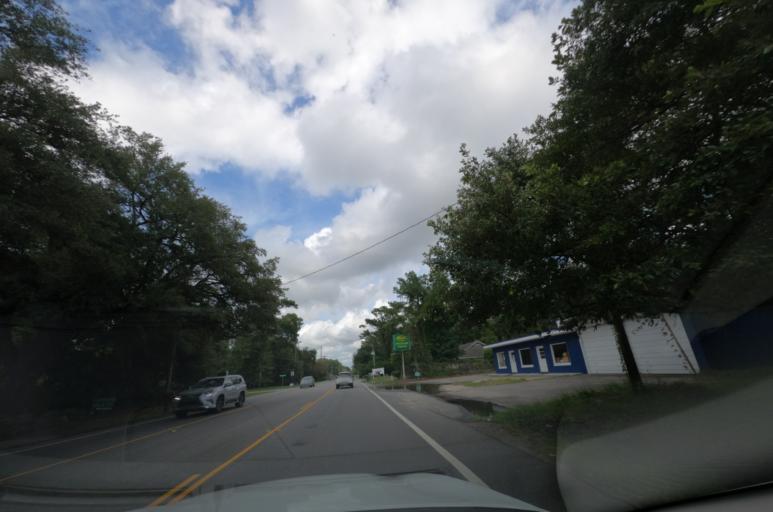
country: US
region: South Carolina
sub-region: Charleston County
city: Shell Point
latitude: 32.7338
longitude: -80.0566
